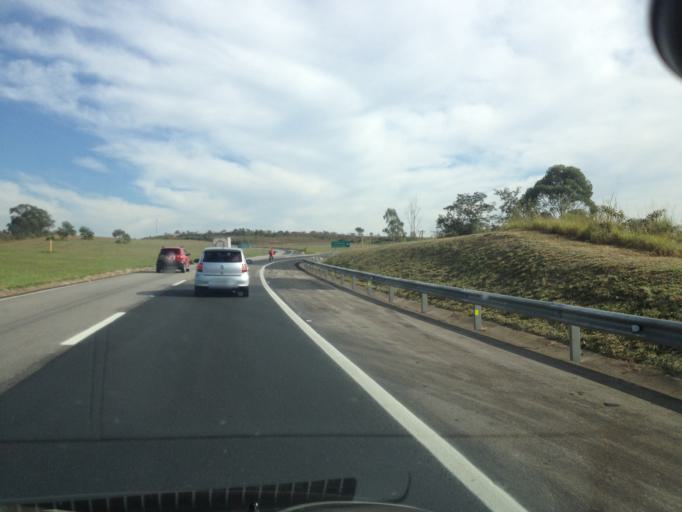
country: BR
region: Sao Paulo
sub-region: Itu
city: Itu
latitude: -23.4016
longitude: -47.3295
